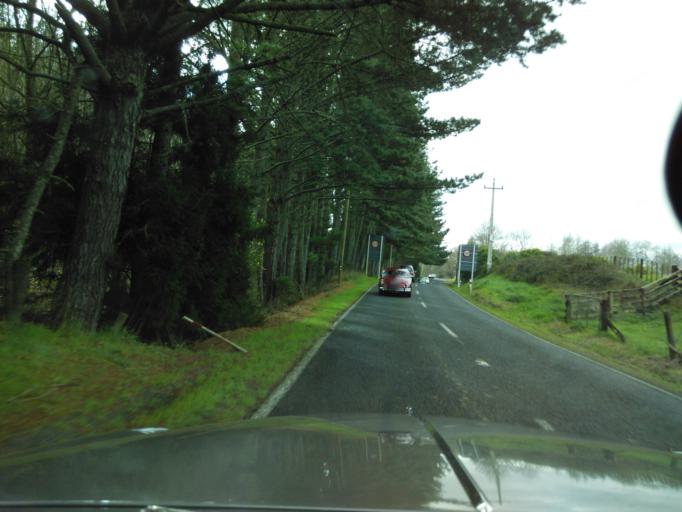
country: NZ
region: Auckland
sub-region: Auckland
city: Red Hill
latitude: -37.1381
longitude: 175.0406
